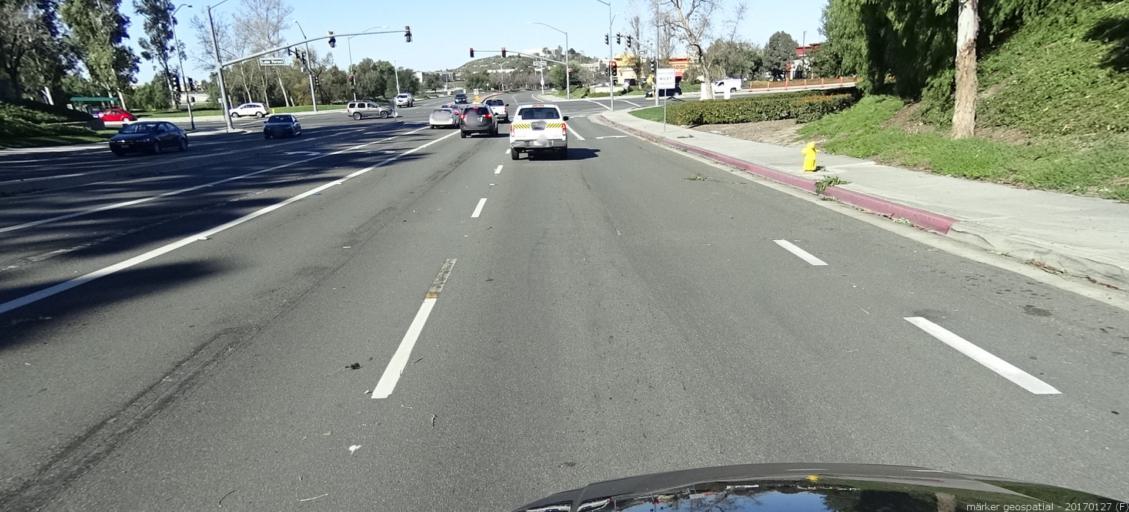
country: US
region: California
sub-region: Orange County
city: Foothill Ranch
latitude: 33.6690
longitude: -117.6605
